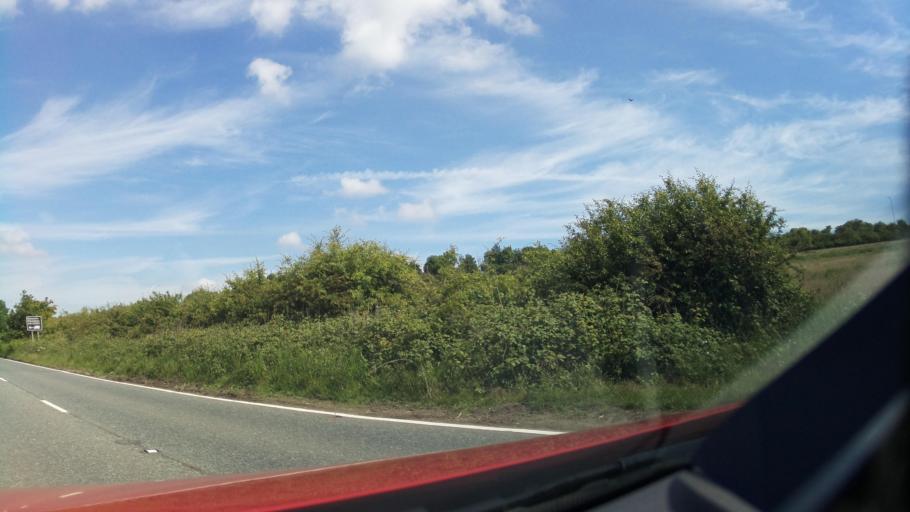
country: GB
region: England
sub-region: North Lincolnshire
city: Broughton
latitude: 53.5528
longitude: -0.5829
